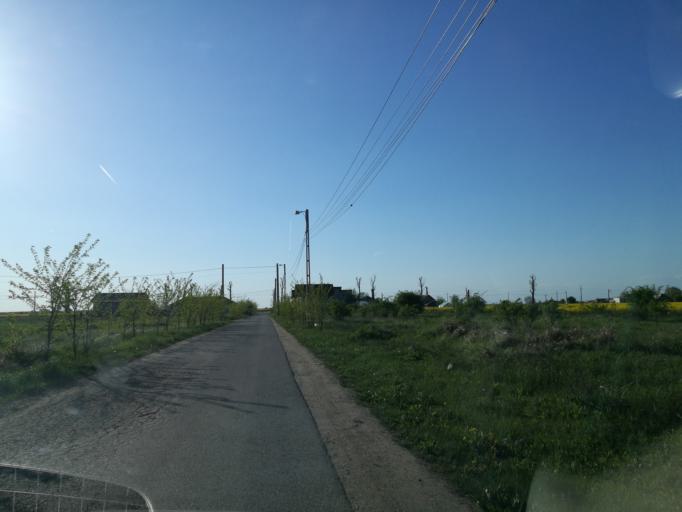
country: RO
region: Ilfov
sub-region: Comuna Vidra
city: Vidra
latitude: 44.2805
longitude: 26.1823
